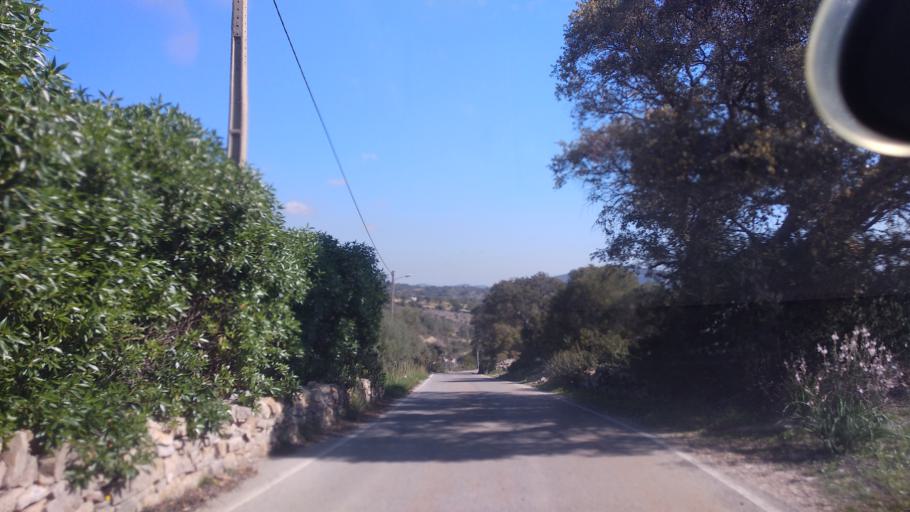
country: PT
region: Faro
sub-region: Faro
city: Santa Barbara de Nexe
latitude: 37.1112
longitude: -7.9329
